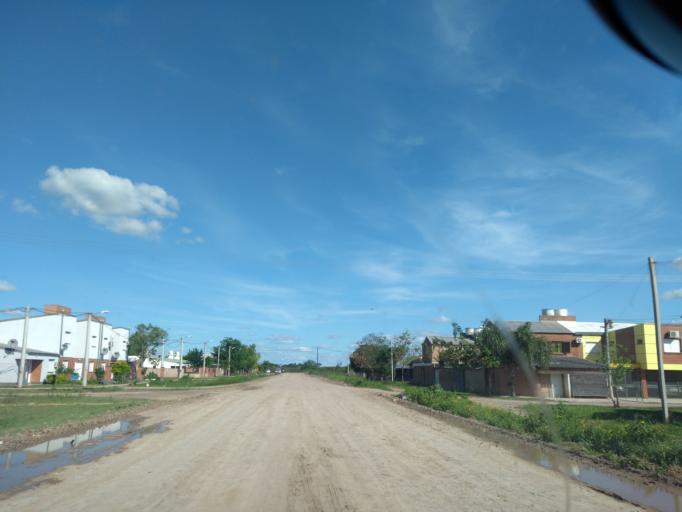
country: AR
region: Chaco
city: Resistencia
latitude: -27.4517
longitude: -58.9630
